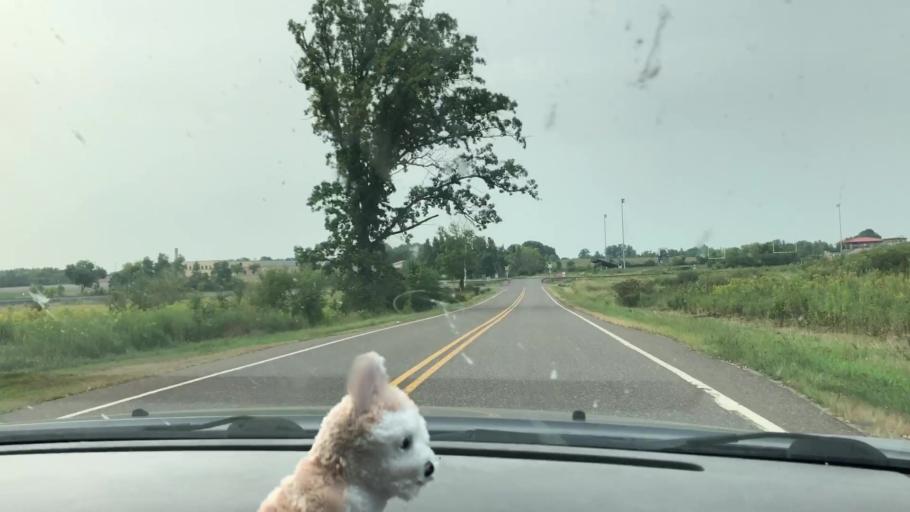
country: US
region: Wisconsin
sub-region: Chippewa County
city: Stanley
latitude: 44.9568
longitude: -90.9223
